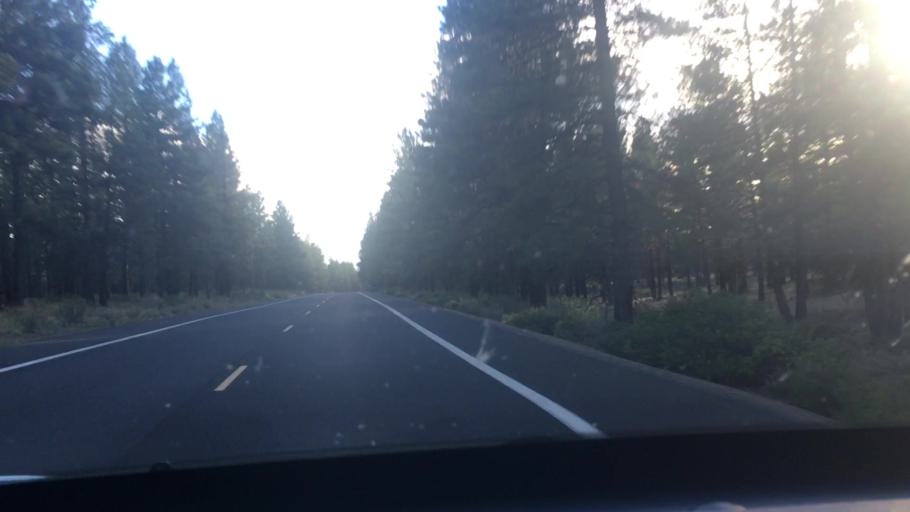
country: US
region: Oregon
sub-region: Deschutes County
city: Deschutes River Woods
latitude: 44.0460
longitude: -121.3995
